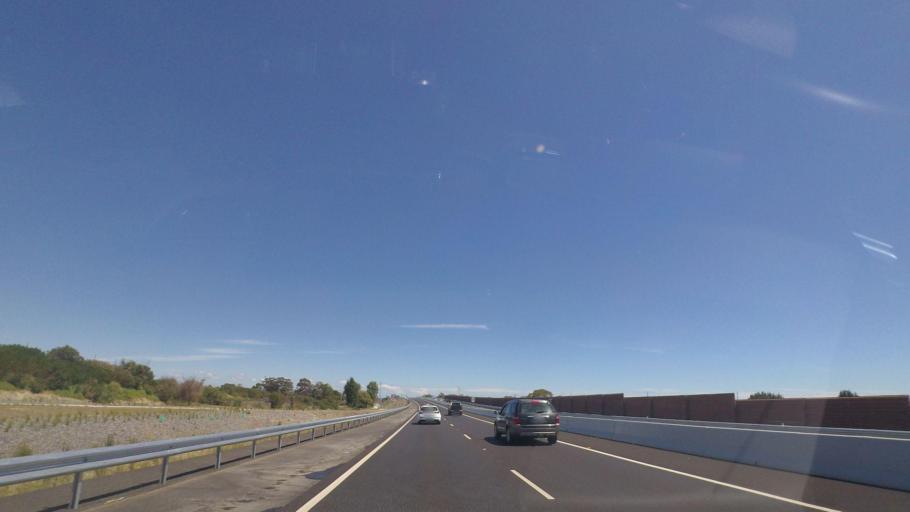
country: AU
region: Victoria
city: Heatherton
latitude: -37.9669
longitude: 145.1169
